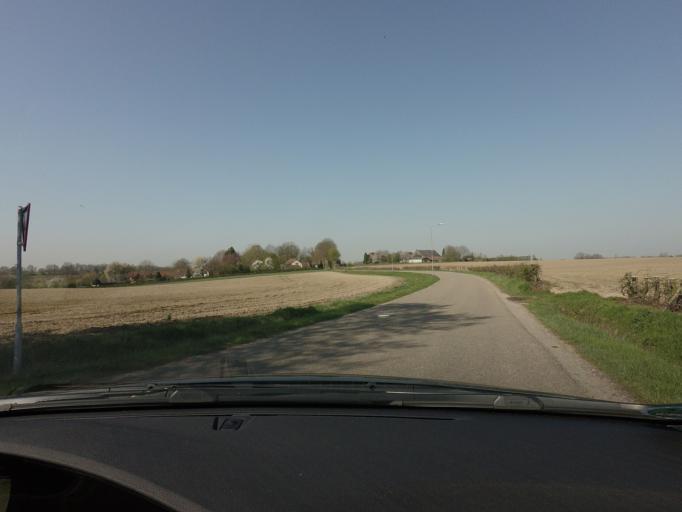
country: NL
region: Limburg
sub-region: Eijsden-Margraten
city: Margraten
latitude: 50.8311
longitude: 5.8196
